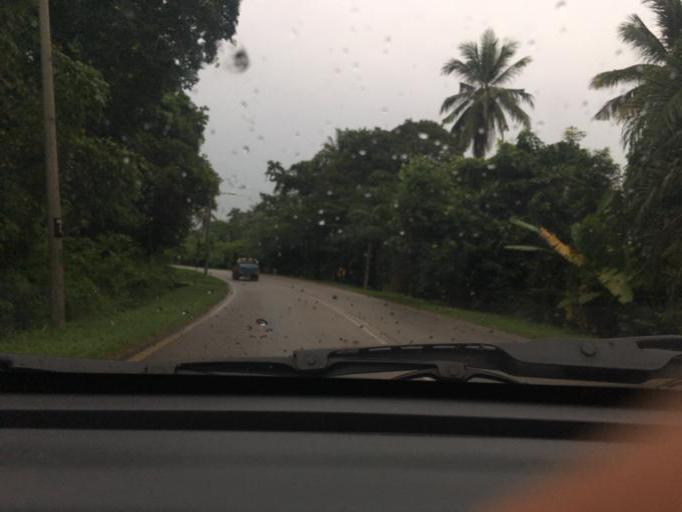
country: MY
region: Kedah
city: Bedong
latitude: 5.6946
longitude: 100.6322
